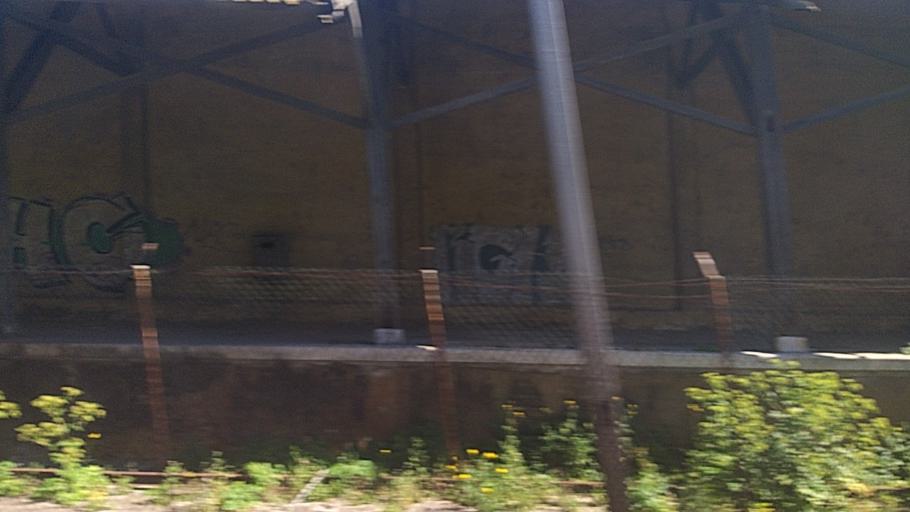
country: PT
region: Lisbon
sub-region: Lisbon
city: Lisbon
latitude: 38.7401
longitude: -9.1054
